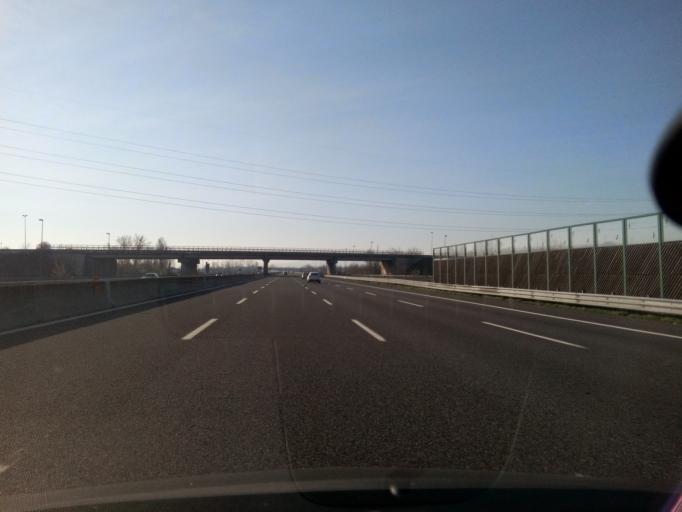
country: IT
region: Emilia-Romagna
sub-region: Provincia di Modena
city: Baggiovara
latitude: 44.6304
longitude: 10.8772
